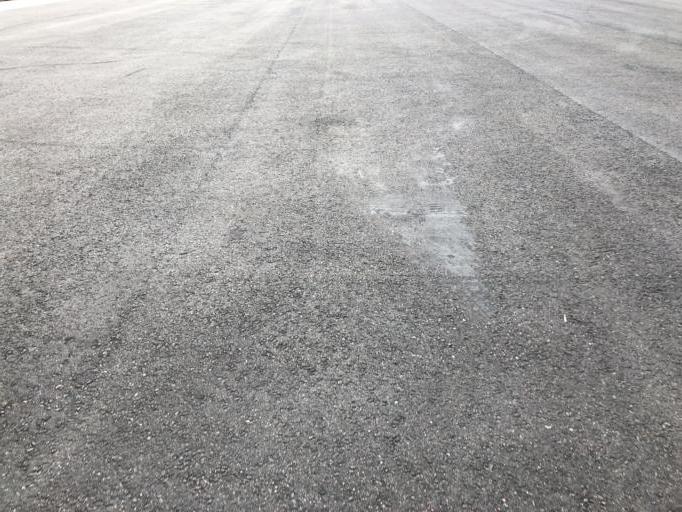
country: SE
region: Vaestra Goetaland
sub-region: Goteborg
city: Majorna
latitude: 57.7399
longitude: 11.8641
